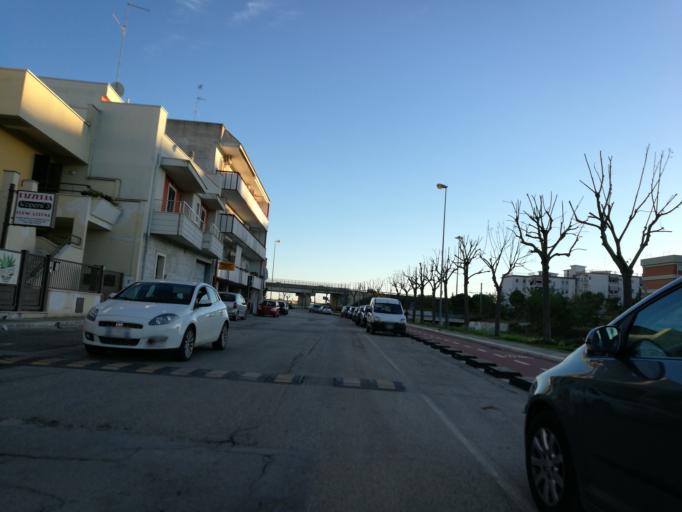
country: IT
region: Apulia
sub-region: Provincia di Bari
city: Adelfia
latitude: 40.9998
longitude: 16.8734
